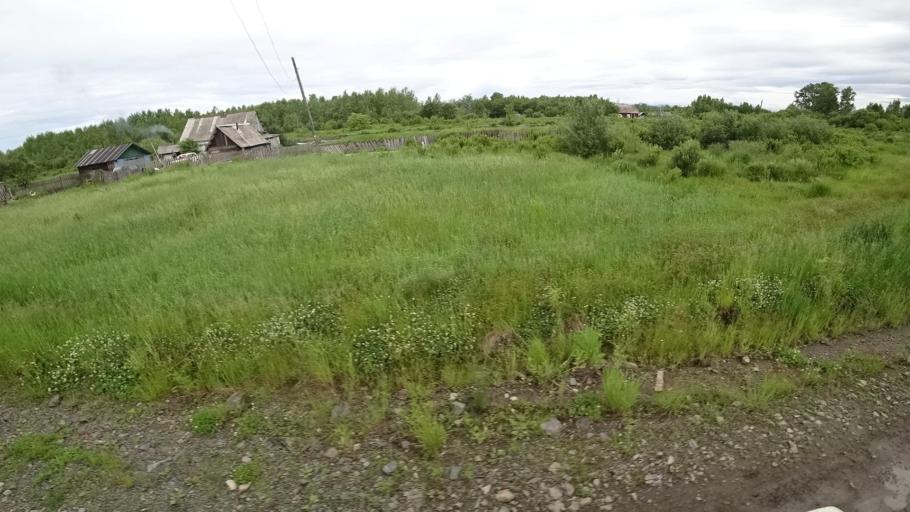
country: RU
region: Khabarovsk Krai
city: Amursk
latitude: 49.8842
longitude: 136.1284
